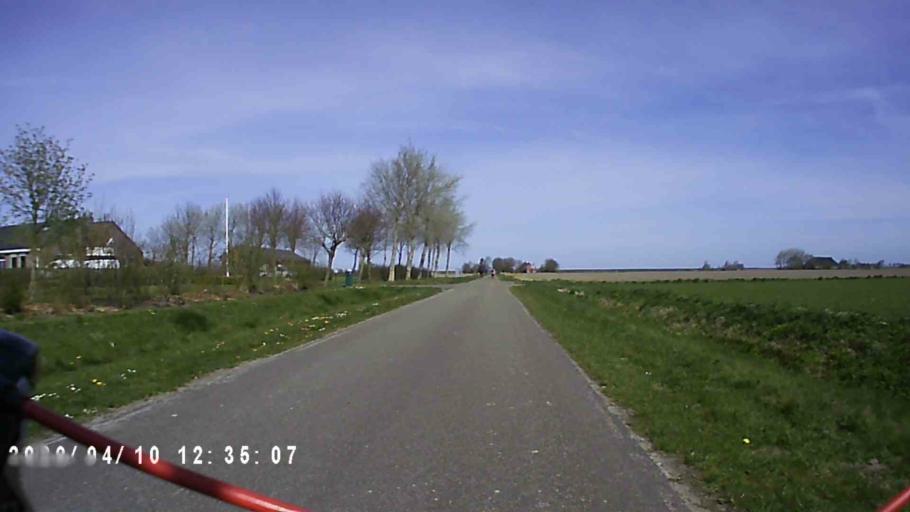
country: NL
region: Groningen
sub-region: Gemeente De Marne
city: Ulrum
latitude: 53.3989
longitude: 6.4171
